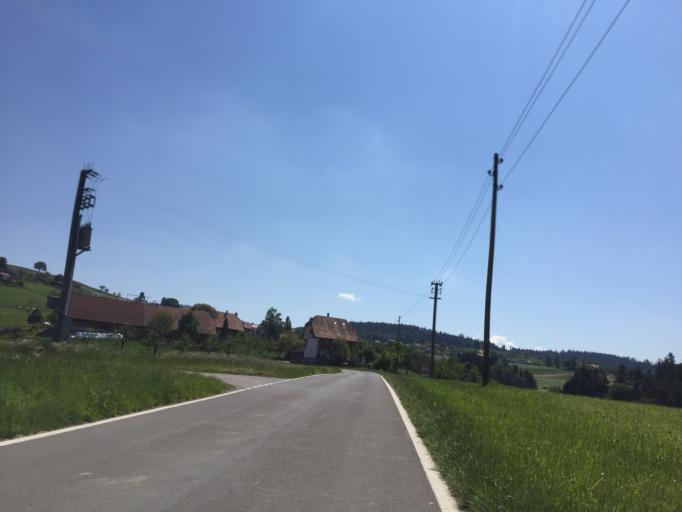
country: CH
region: Bern
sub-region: Bern-Mittelland District
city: Taegertschi
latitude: 46.8607
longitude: 7.5947
